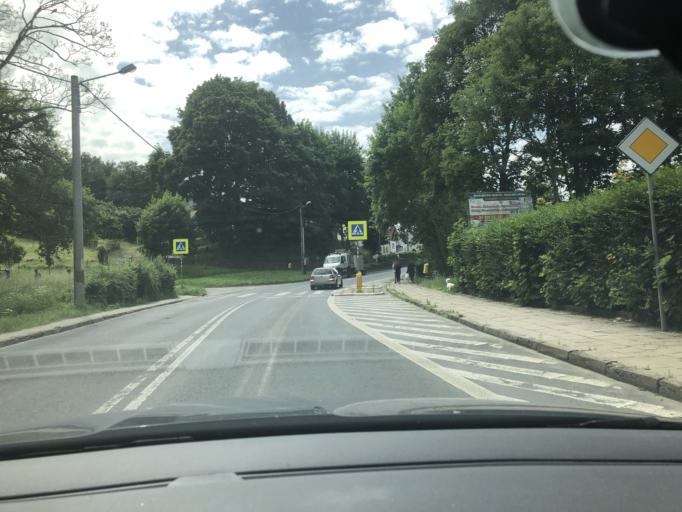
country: PL
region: Lower Silesian Voivodeship
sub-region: Powiat zlotoryjski
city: Zlotoryja
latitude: 51.1294
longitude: 15.9284
